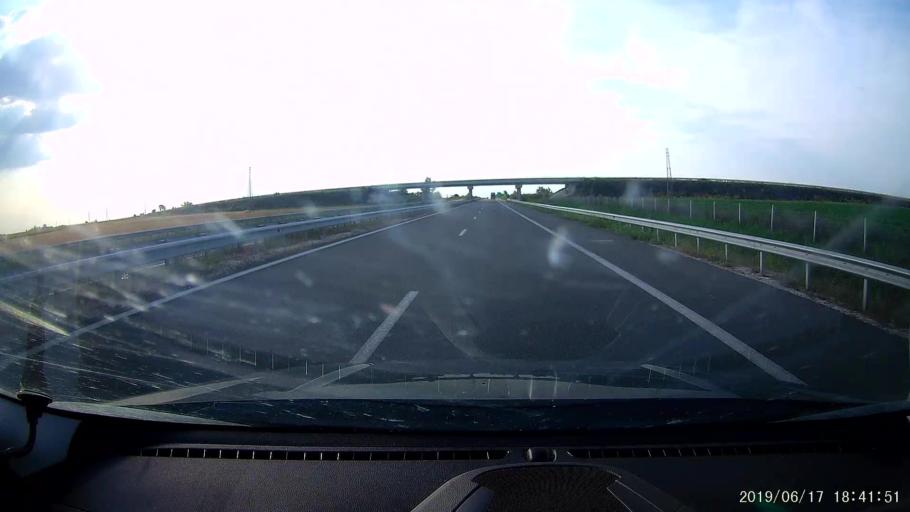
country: BG
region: Stara Zagora
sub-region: Obshtina Chirpan
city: Chirpan
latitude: 42.1801
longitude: 25.2481
